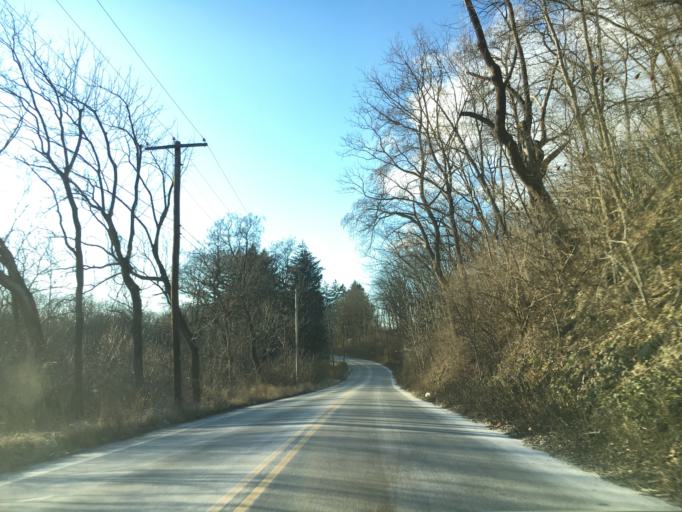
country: US
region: Pennsylvania
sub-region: Lehigh County
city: Egypt
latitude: 40.6735
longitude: -75.5188
